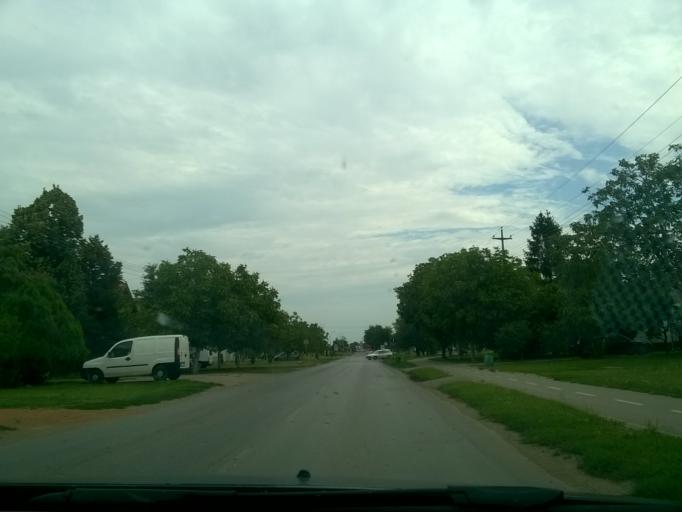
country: RS
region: Autonomna Pokrajina Vojvodina
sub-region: Srednjebanatski Okrug
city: Zrenjanin
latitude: 45.3957
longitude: 20.3999
